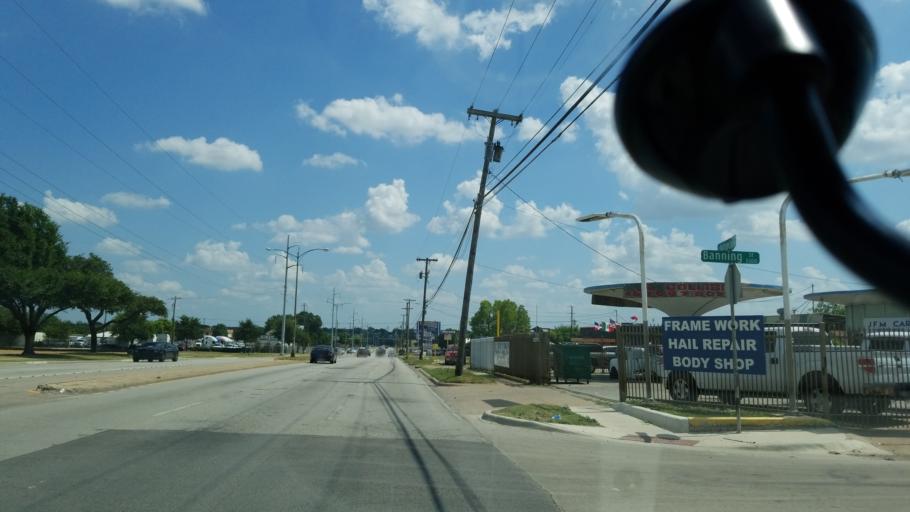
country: US
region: Texas
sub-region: Dallas County
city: Cockrell Hill
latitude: 32.7170
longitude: -96.8744
